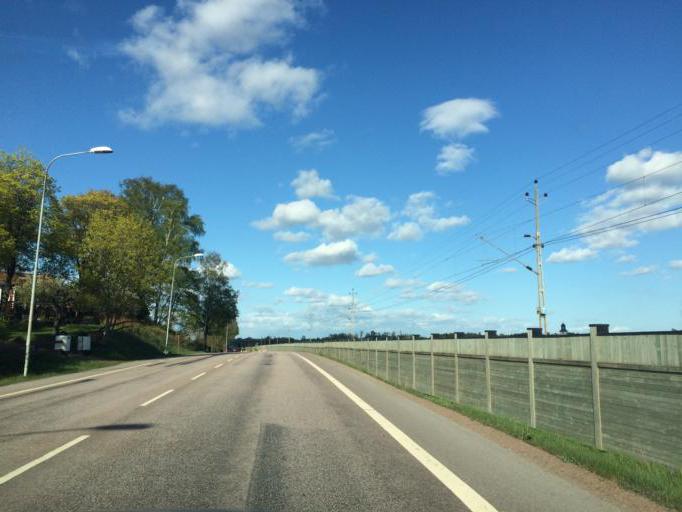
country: SE
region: Vaestmanland
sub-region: Hallstahammars Kommun
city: Kolback
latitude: 59.5570
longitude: 16.2155
